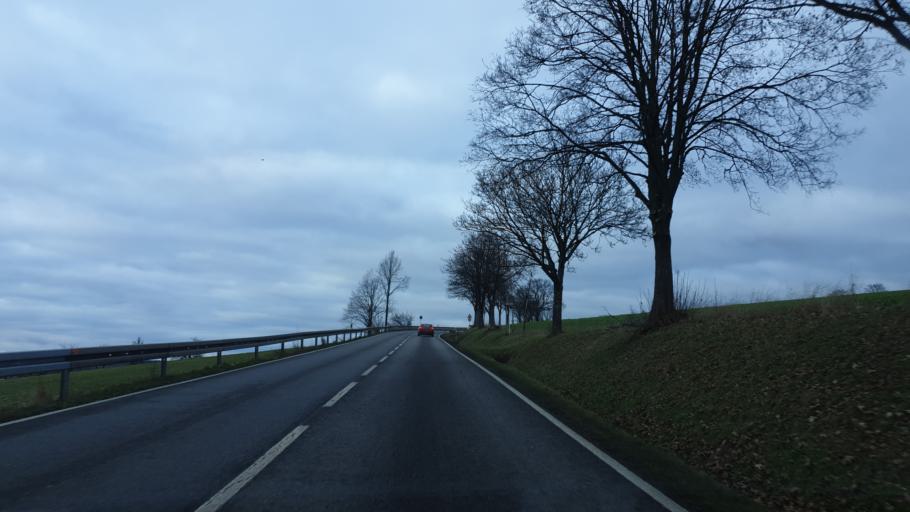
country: DE
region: Saxony
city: Mulsen
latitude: 50.7402
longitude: 12.5764
